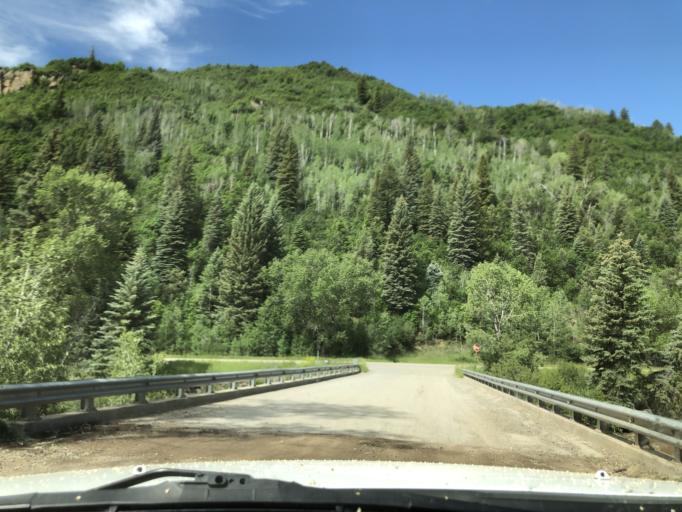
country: US
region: Colorado
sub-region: Delta County
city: Paonia
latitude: 38.9897
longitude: -107.3487
